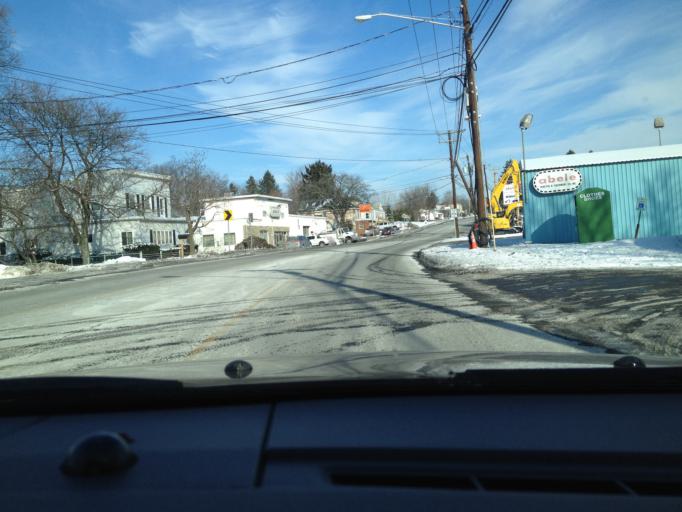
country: US
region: New York
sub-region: Albany County
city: West Albany
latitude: 42.6915
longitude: -73.7773
